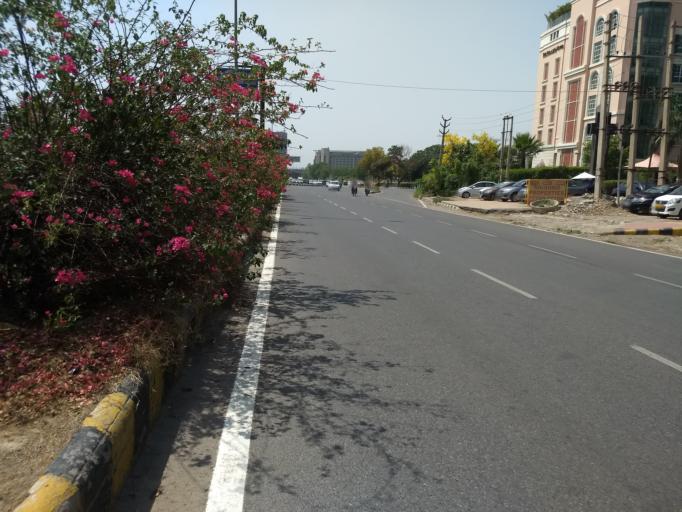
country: IN
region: Haryana
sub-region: Gurgaon
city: Gurgaon
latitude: 28.4637
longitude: 77.0643
